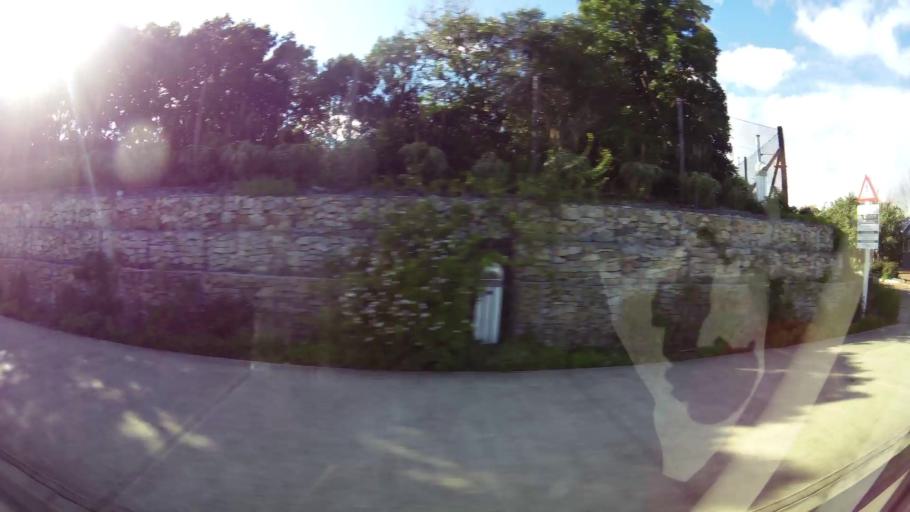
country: ZA
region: Western Cape
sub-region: Eden District Municipality
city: Knysna
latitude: -34.0460
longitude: 23.0478
